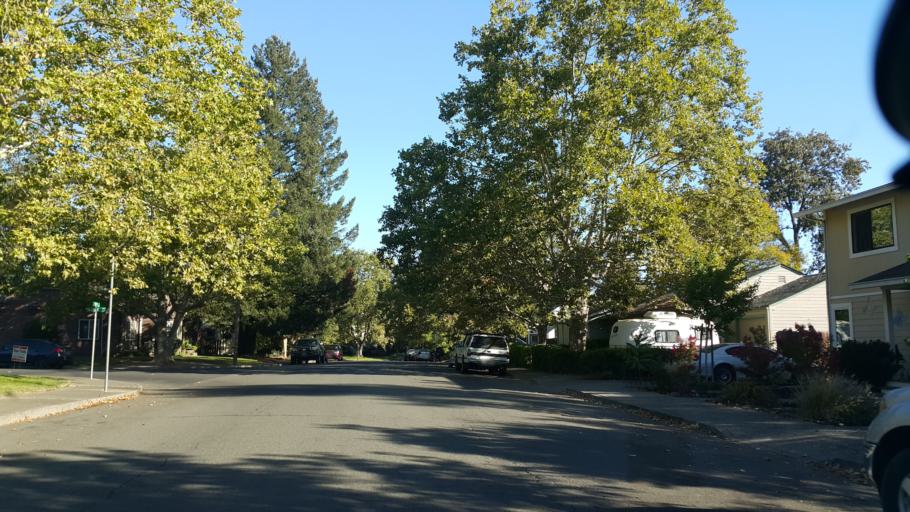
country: US
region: California
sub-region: Mendocino County
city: Ukiah
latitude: 39.1418
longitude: -123.2137
